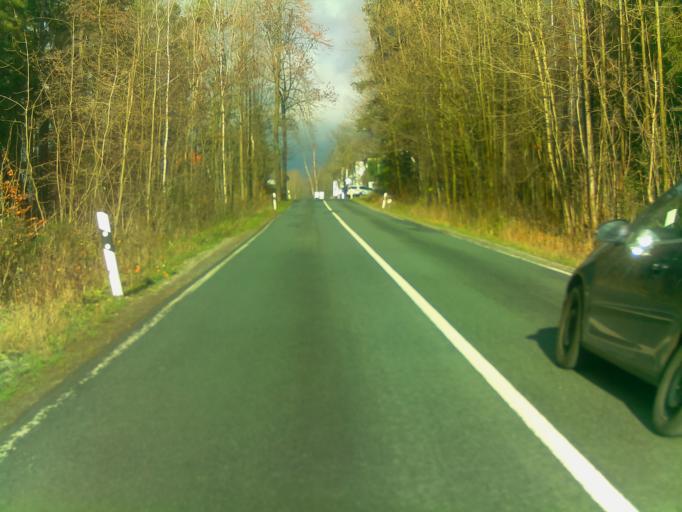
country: DE
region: Thuringia
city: Schleusingen
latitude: 50.4854
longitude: 10.8376
